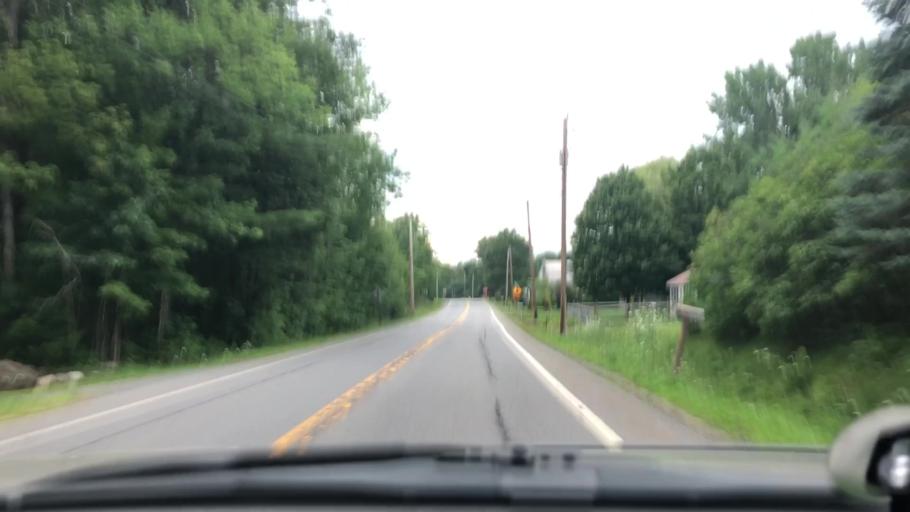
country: US
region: New York
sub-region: Saratoga County
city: Corinth
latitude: 43.2114
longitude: -73.7958
